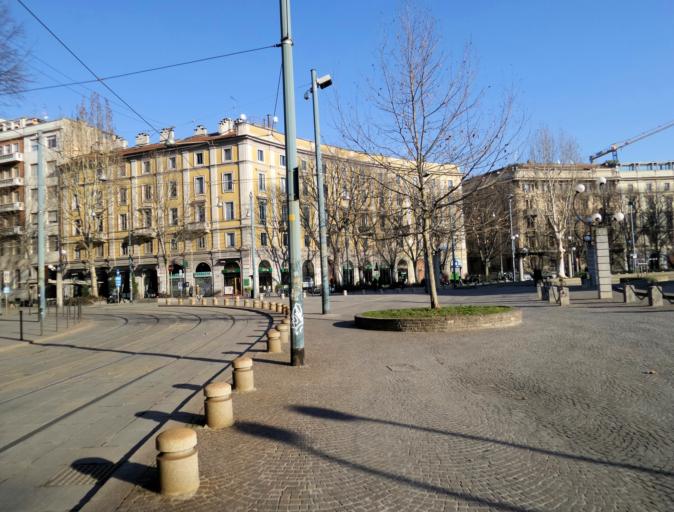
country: IT
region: Lombardy
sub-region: Citta metropolitana di Milano
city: Milano
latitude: 45.4758
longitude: 9.1716
